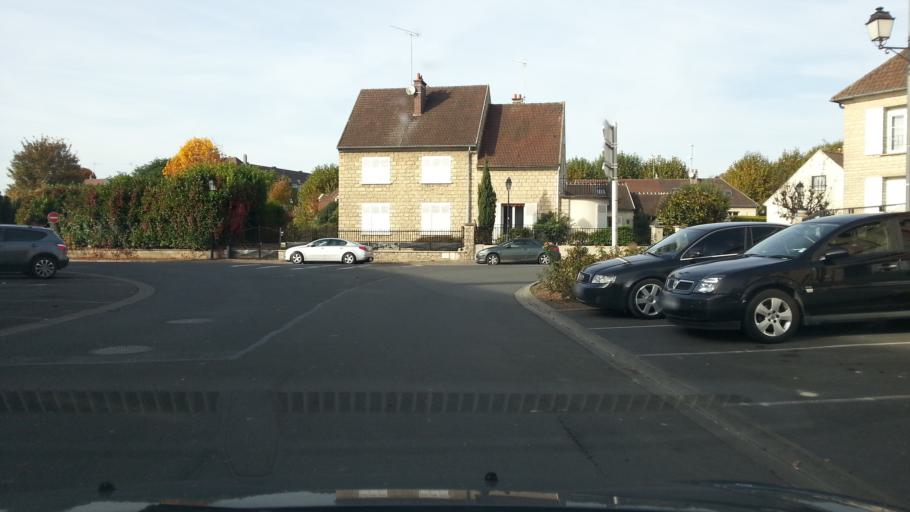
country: FR
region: Picardie
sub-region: Departement de l'Oise
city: Villers-sous-Saint-Leu
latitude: 49.2149
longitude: 2.4192
